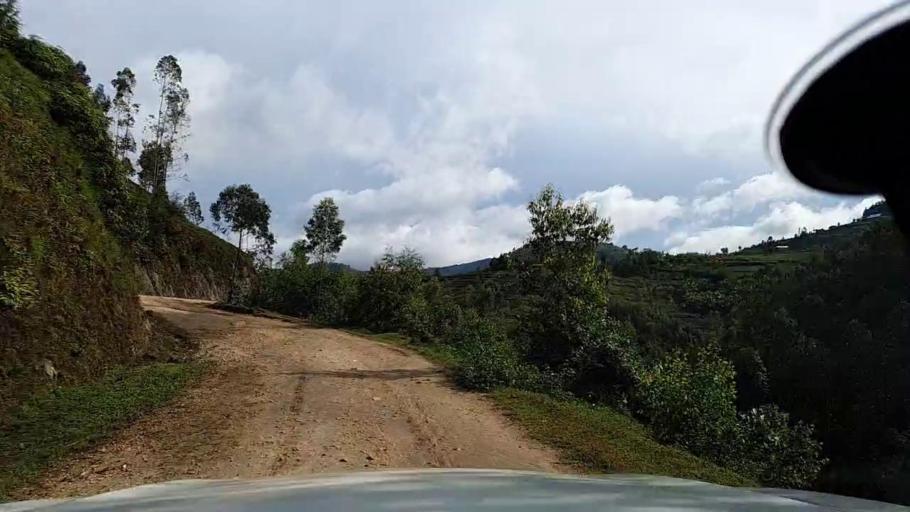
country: RW
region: Western Province
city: Kibuye
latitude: -2.1248
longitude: 29.4976
